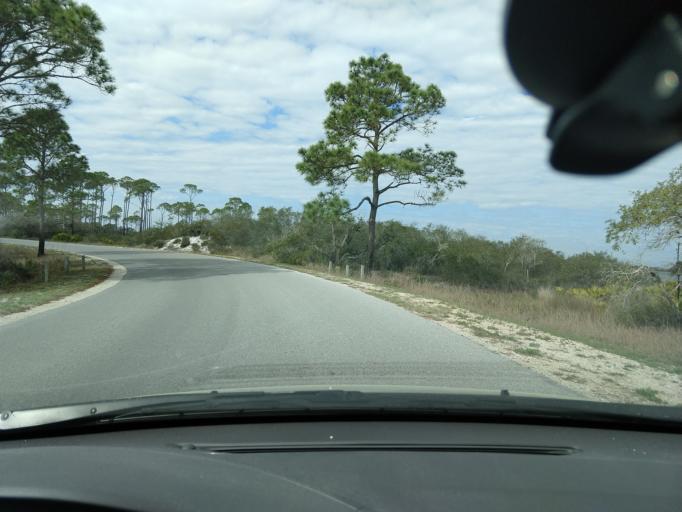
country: US
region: Florida
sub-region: Gulf County
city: Port Saint Joe
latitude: 29.7637
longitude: -85.3980
